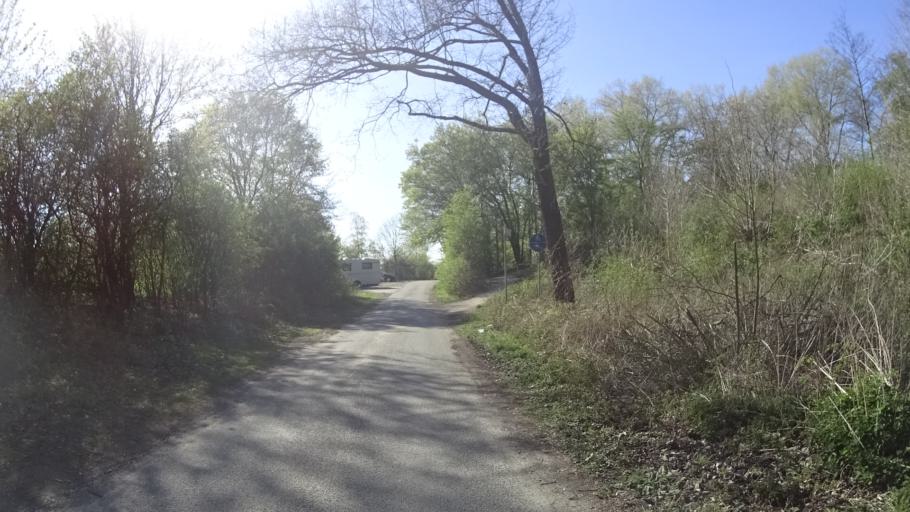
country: DE
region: North Rhine-Westphalia
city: Dorsten
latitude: 51.6636
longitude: 6.9918
